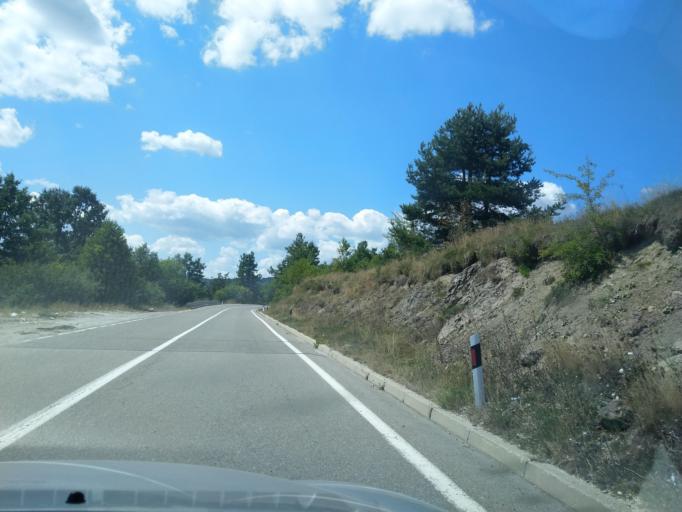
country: RS
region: Central Serbia
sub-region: Zlatiborski Okrug
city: Sjenica
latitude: 43.3064
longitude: 19.9267
